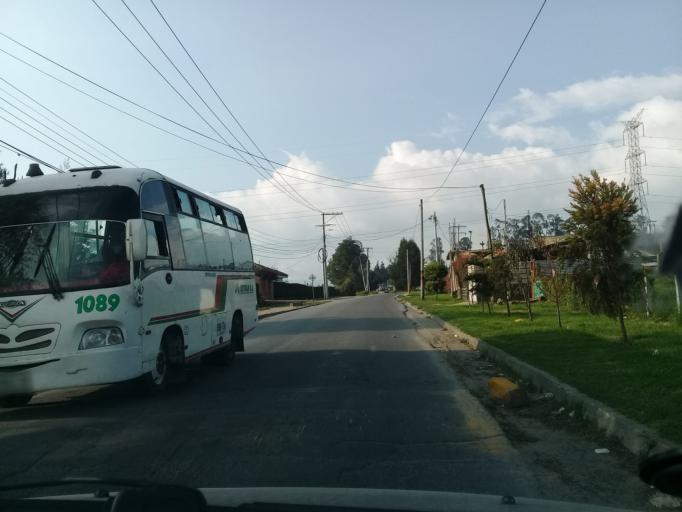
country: CO
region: Cundinamarca
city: Funza
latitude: 4.7352
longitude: -74.2226
